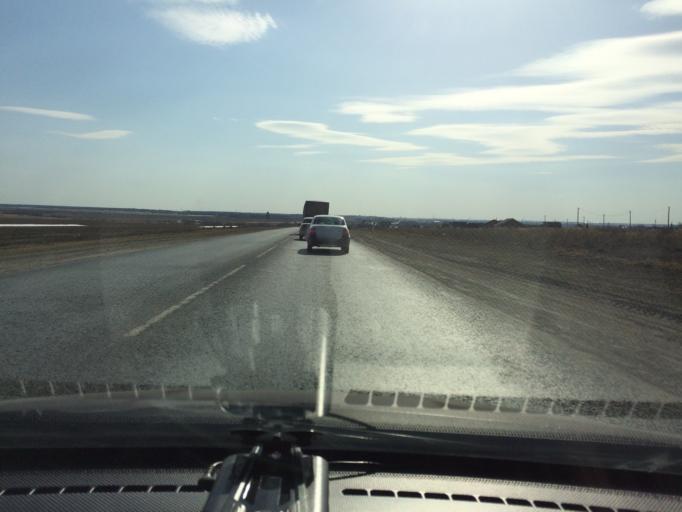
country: RU
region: Mariy-El
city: Yoshkar-Ola
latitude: 56.6962
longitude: 48.0600
